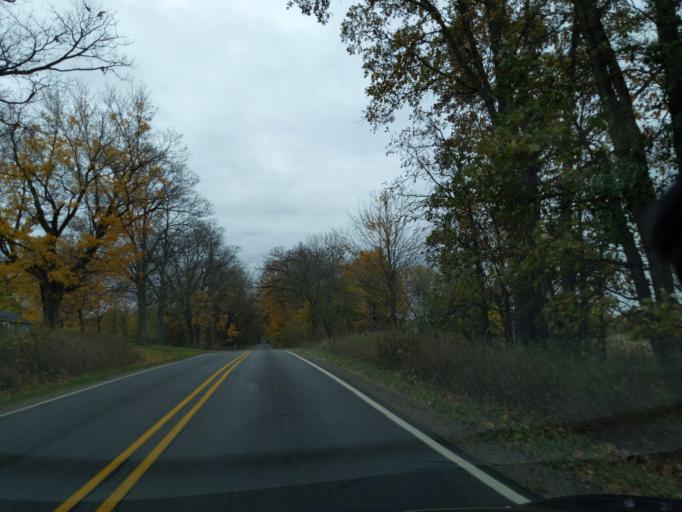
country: US
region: Michigan
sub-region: Jackson County
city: Spring Arbor
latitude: 42.2896
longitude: -84.6001
